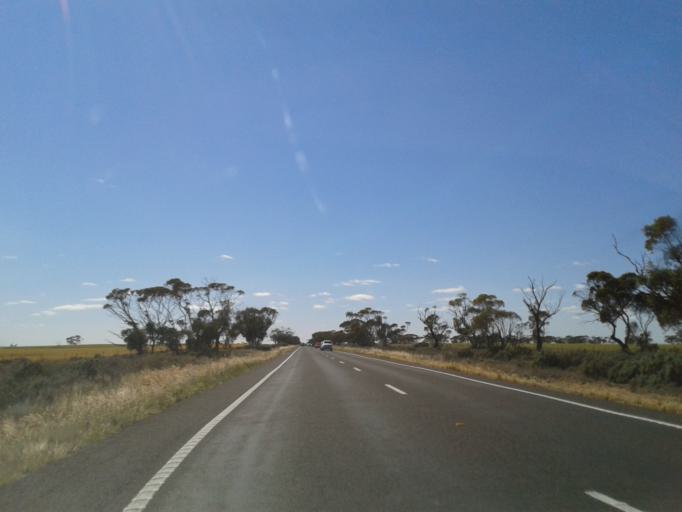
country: AU
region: New South Wales
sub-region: Wentworth
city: Dareton
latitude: -34.2767
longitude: 141.7625
